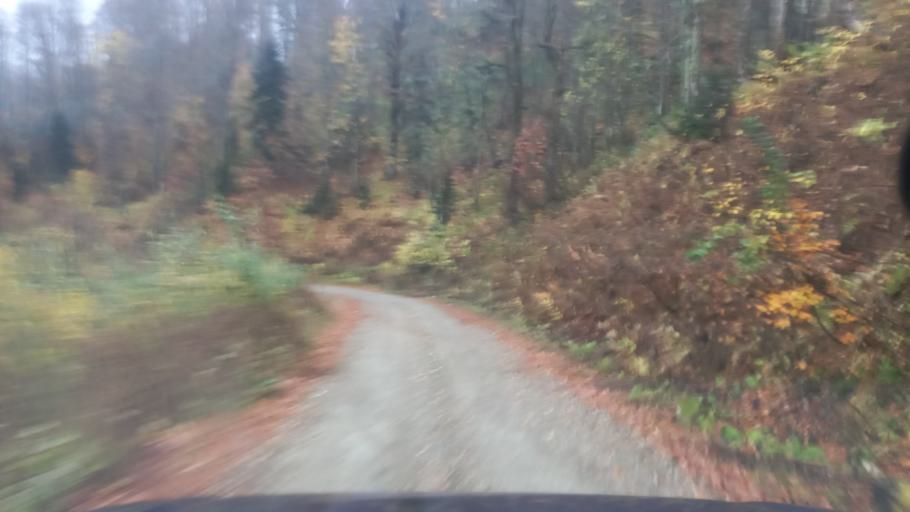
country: RU
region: Krasnodarskiy
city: Dagomys
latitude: 43.9904
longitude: 39.8529
